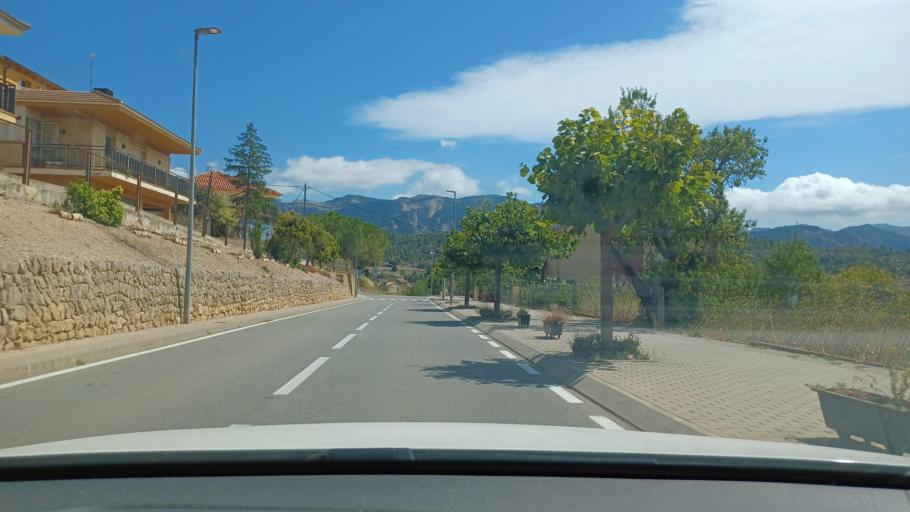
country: ES
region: Catalonia
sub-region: Provincia de Tarragona
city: Horta de Sant Joan
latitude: 40.9520
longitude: 0.3164
